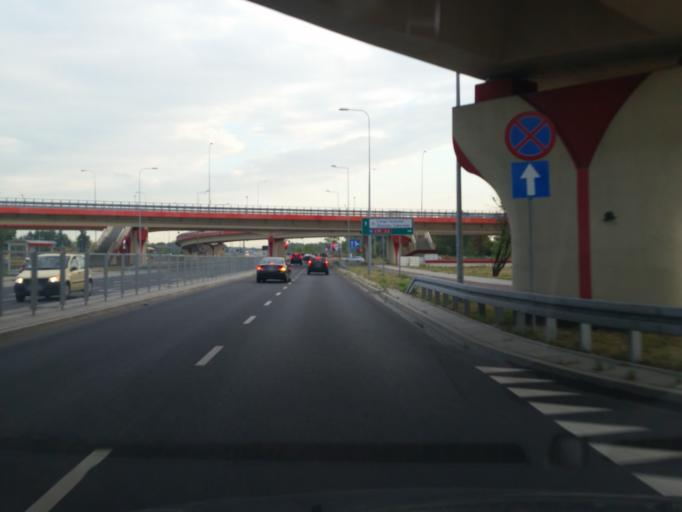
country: PL
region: Masovian Voivodeship
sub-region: Warszawa
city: Wlochy
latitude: 52.1687
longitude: 20.9853
